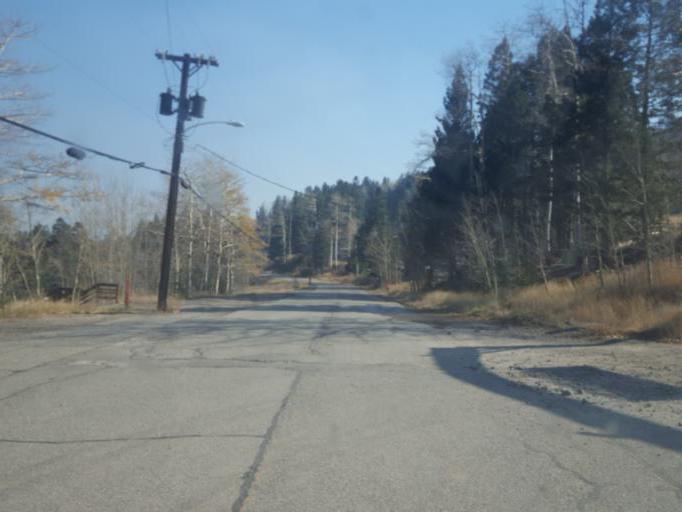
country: US
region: New Mexico
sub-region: Los Alamos County
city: Los Alamos
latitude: 35.8950
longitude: -106.3904
